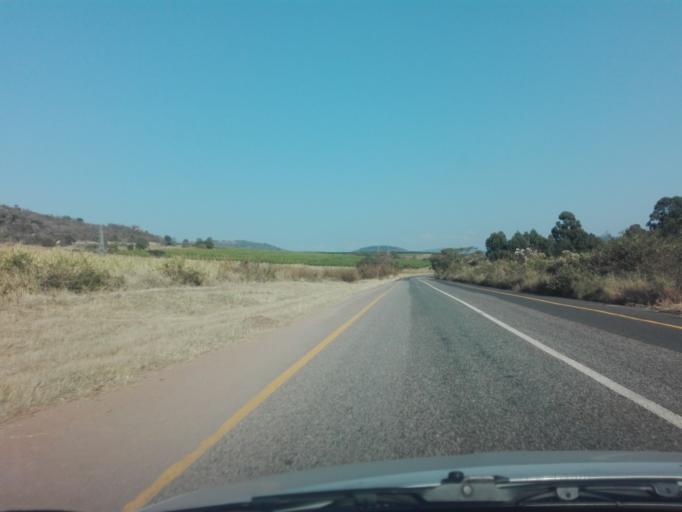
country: ZA
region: Mpumalanga
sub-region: Ehlanzeni District
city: Nelspruit
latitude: -25.5110
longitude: 30.9117
